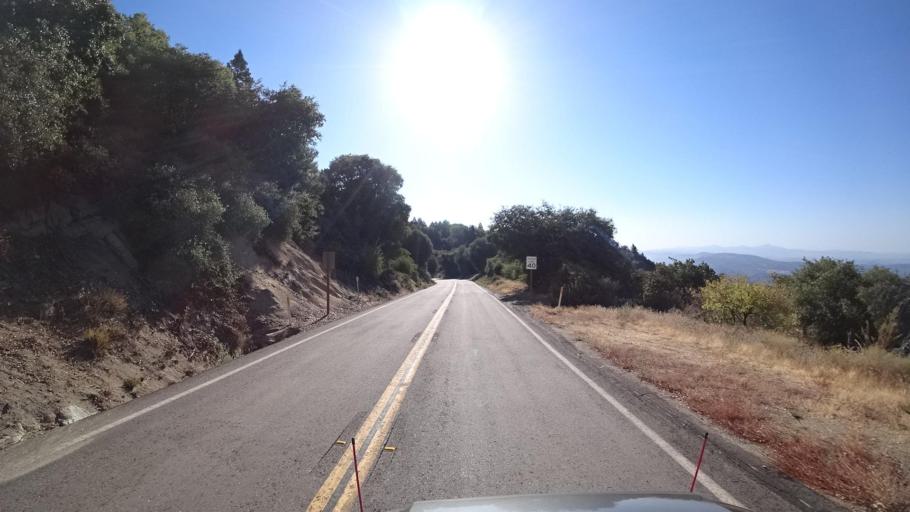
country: US
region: California
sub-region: Riverside County
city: Aguanga
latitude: 33.3019
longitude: -116.8454
